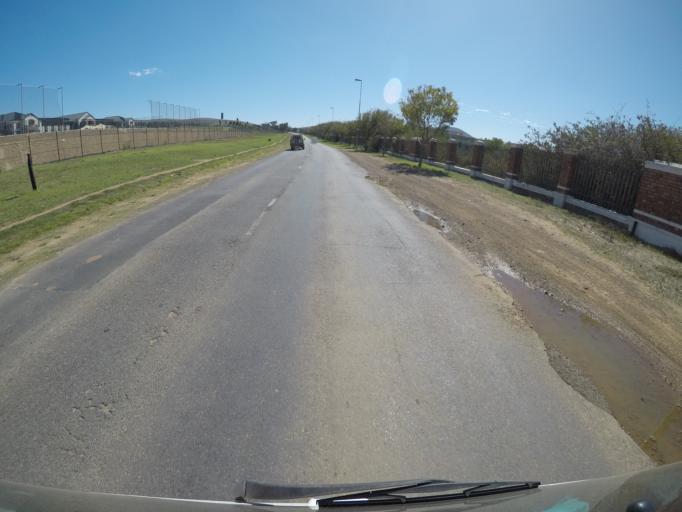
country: ZA
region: Western Cape
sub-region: City of Cape Town
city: Kraaifontein
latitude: -33.8154
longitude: 18.6331
